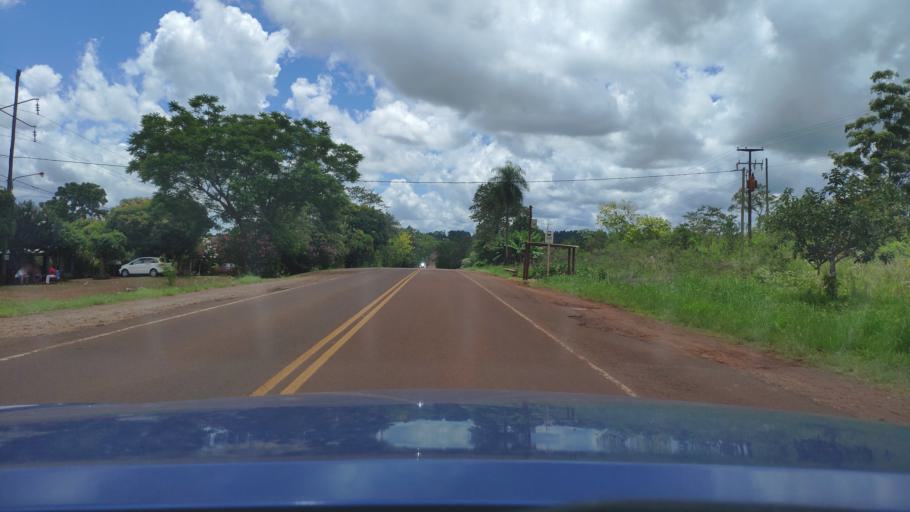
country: AR
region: Misiones
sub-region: Departamento de Leandro N. Alem
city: Leandro N. Alem
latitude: -27.6381
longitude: -55.2925
